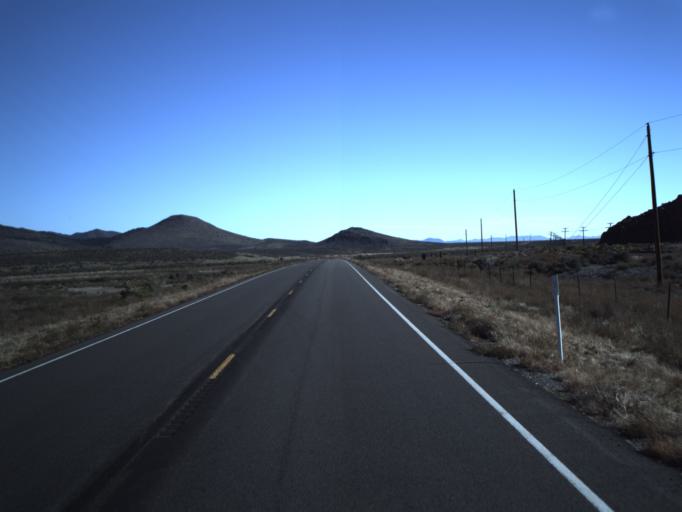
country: US
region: Utah
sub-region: Washington County
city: Enterprise
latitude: 37.7793
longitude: -113.9678
